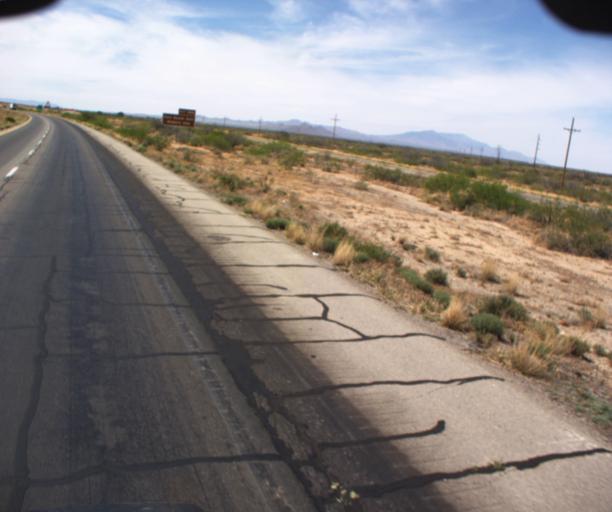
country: US
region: Arizona
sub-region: Cochise County
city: Willcox
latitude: 32.3171
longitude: -109.4403
